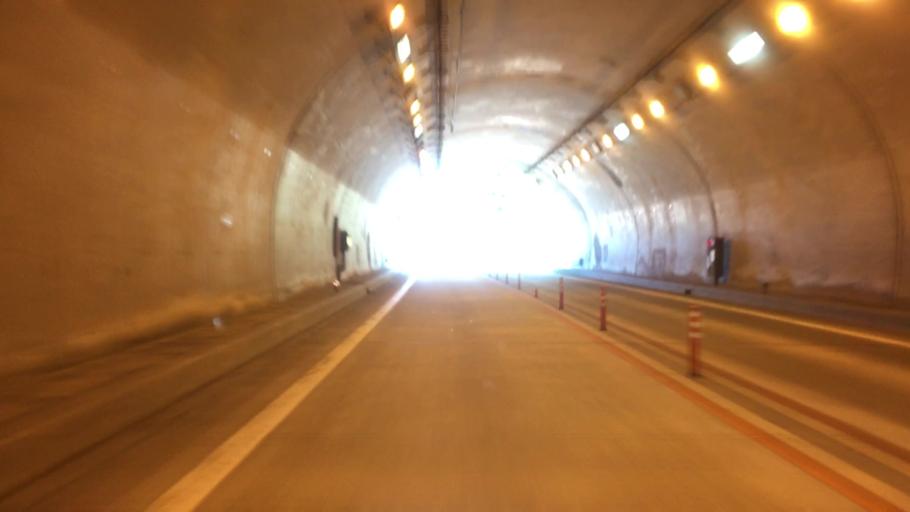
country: JP
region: Tottori
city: Tottori
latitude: 35.4132
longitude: 134.2070
